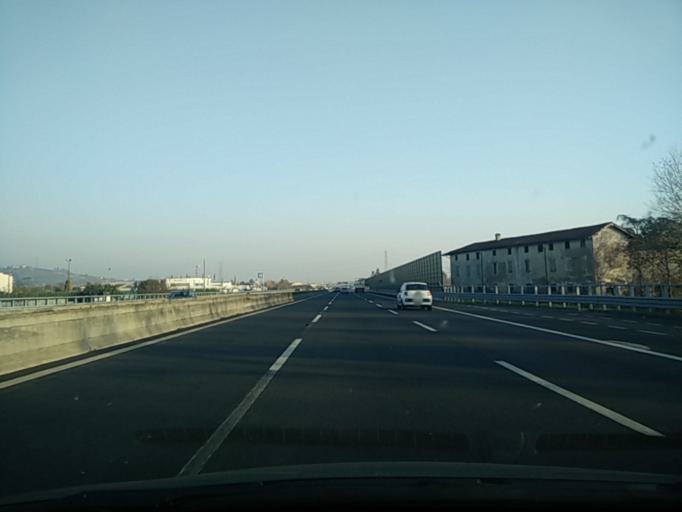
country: IT
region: Lombardy
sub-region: Provincia di Bergamo
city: Telgate
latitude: 45.6367
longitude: 9.8384
